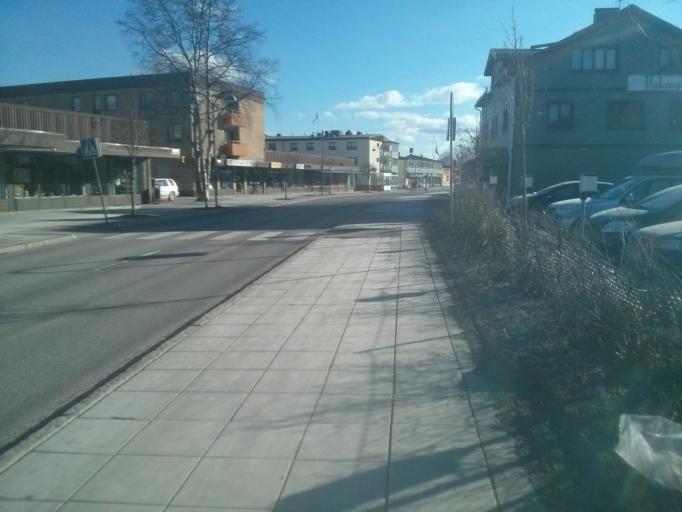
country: SE
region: Vaesternorrland
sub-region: Sundsvalls Kommun
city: Kvissleby
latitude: 62.3001
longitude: 17.3778
